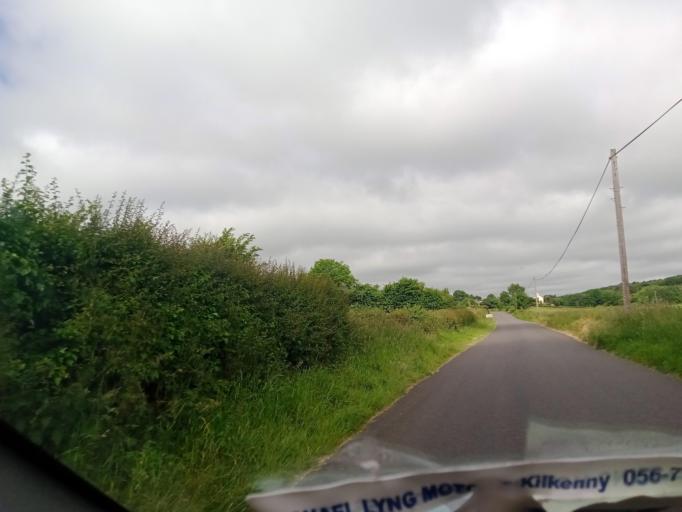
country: IE
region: Leinster
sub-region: Kilkenny
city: Ballyragget
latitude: 52.7651
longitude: -7.4657
